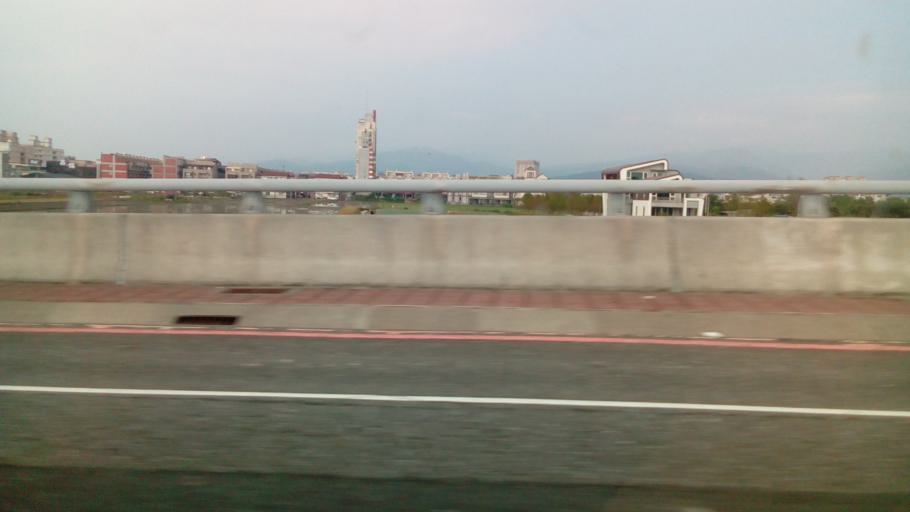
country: TW
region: Taiwan
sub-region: Yilan
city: Yilan
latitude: 24.7580
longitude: 121.7715
